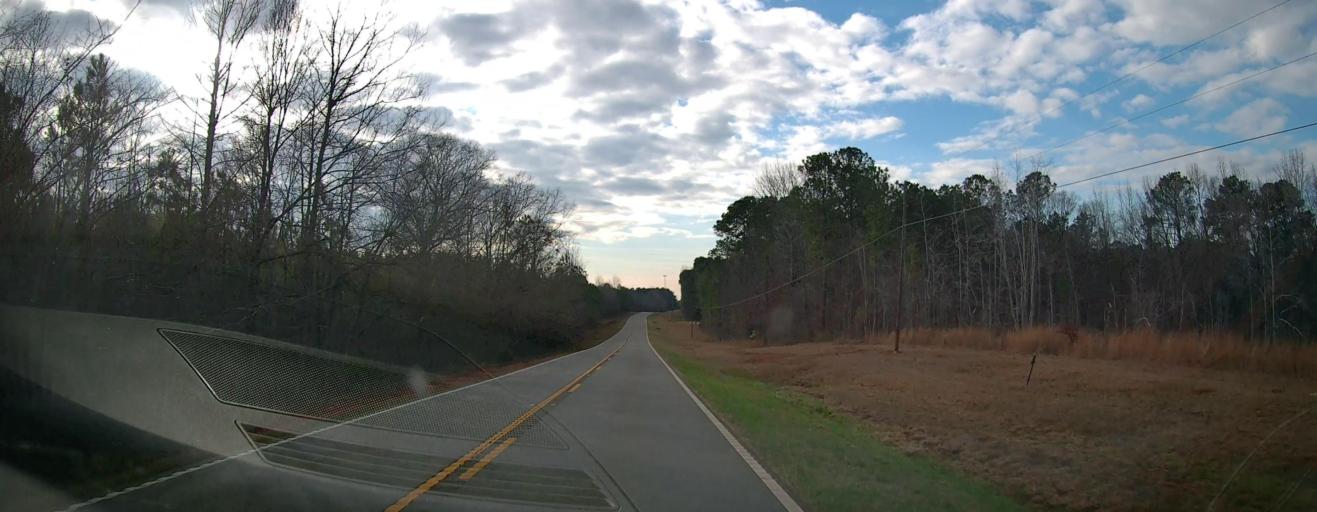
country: US
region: Georgia
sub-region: Harris County
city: Hamilton
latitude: 32.6867
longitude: -84.7748
